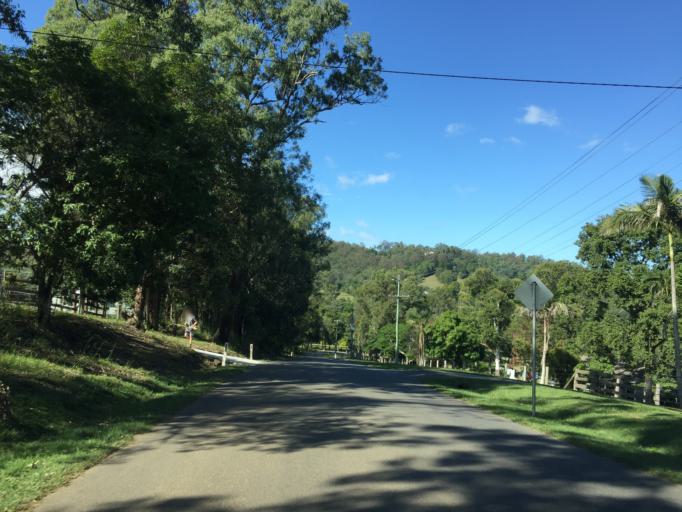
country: AU
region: Queensland
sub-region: Brisbane
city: Kenmore Hills
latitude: -27.4704
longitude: 152.9057
